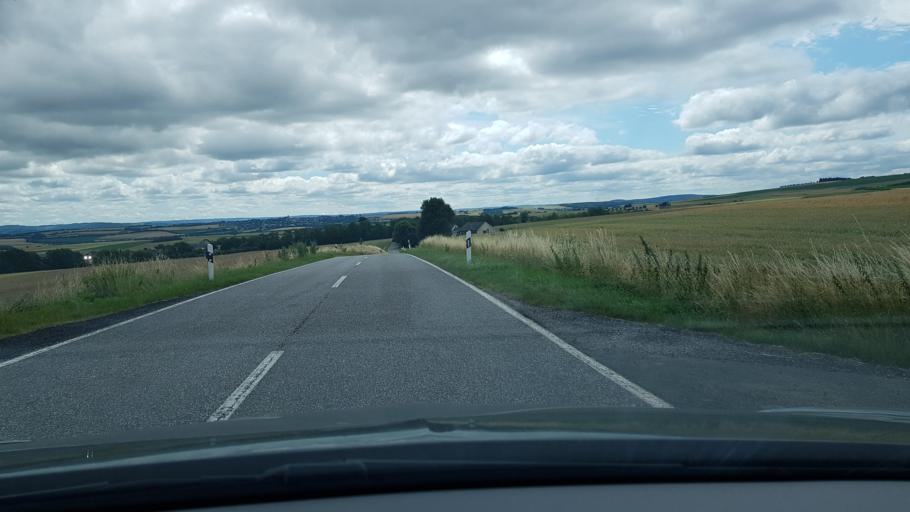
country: DE
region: Rheinland-Pfalz
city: Einig
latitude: 50.2761
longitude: 7.2931
